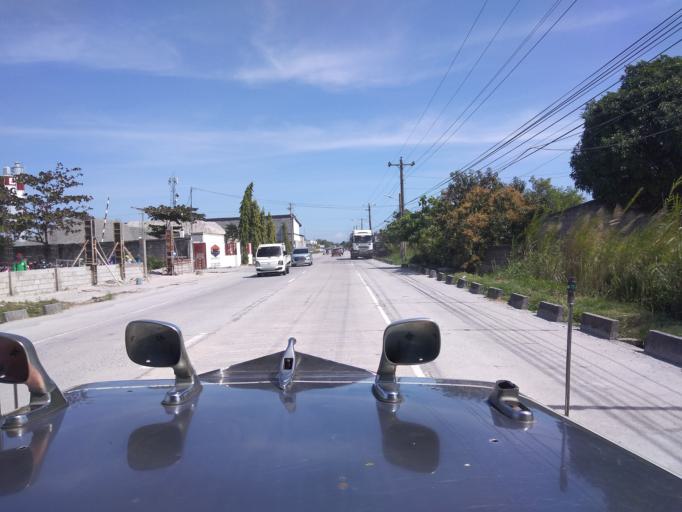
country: PH
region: Central Luzon
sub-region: Province of Pampanga
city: San Juan
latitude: 15.0152
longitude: 120.6664
